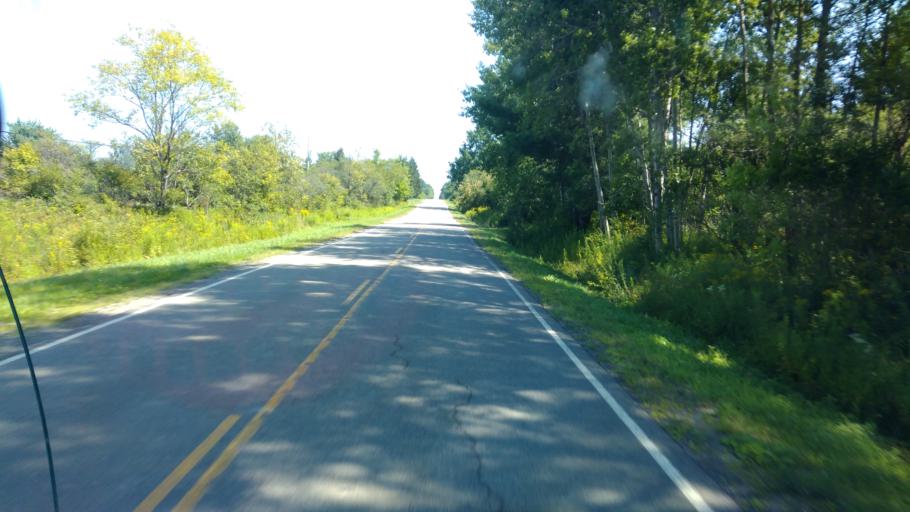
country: US
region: New York
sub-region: Allegany County
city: Alfred
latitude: 42.2933
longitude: -77.9155
